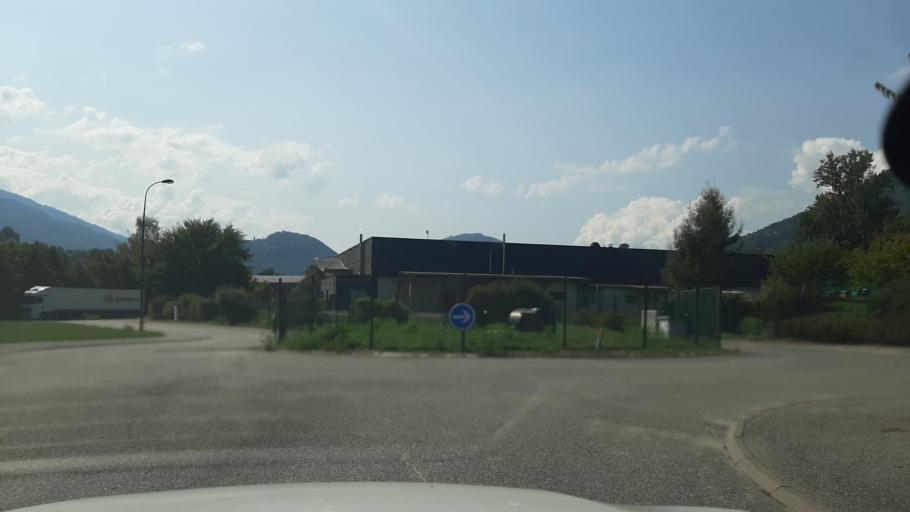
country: FR
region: Rhone-Alpes
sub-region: Departement de la Savoie
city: La Rochette
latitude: 45.4698
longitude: 6.1264
